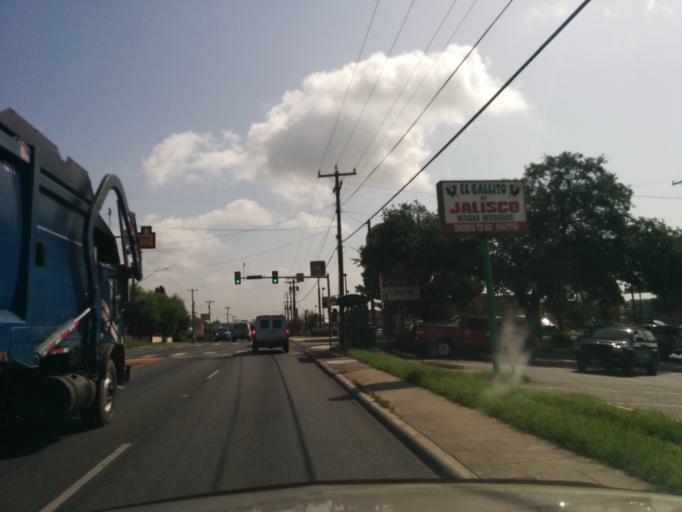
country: US
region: Texas
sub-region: Bexar County
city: Balcones Heights
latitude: 29.5280
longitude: -98.5653
